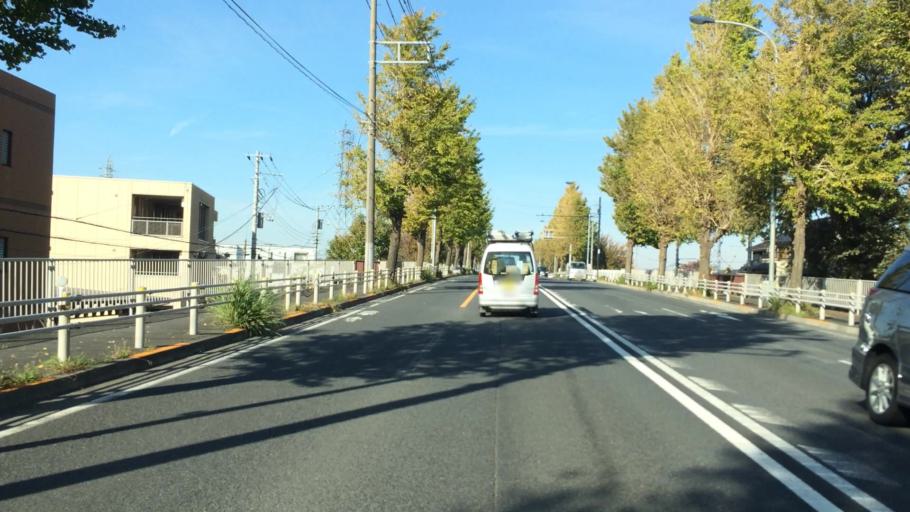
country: JP
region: Tokyo
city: Chofugaoka
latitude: 35.6677
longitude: 139.5142
